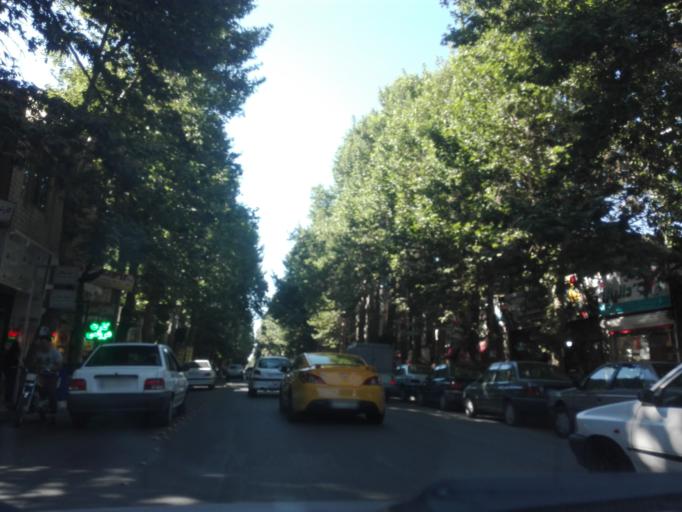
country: IR
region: Tehran
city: Shahriar
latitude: 35.6586
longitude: 51.0583
